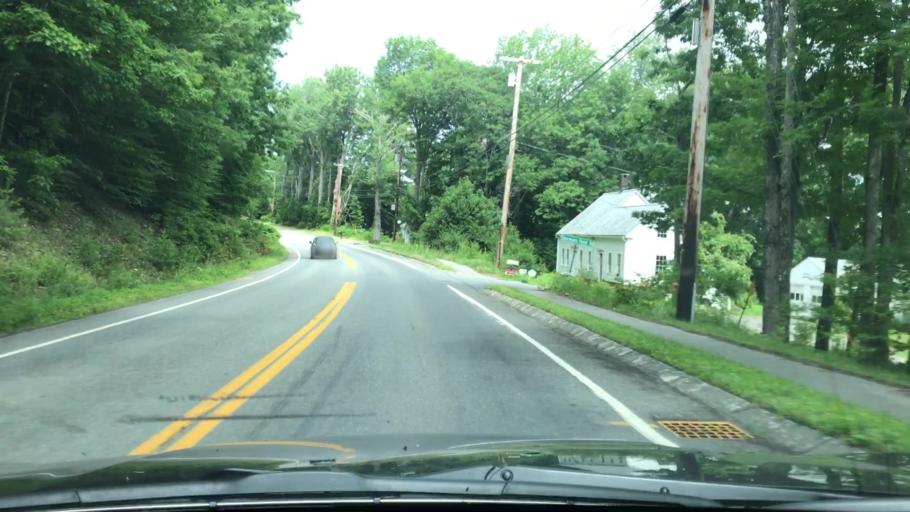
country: US
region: Maine
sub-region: Knox County
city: Camden
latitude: 44.2215
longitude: -69.0527
